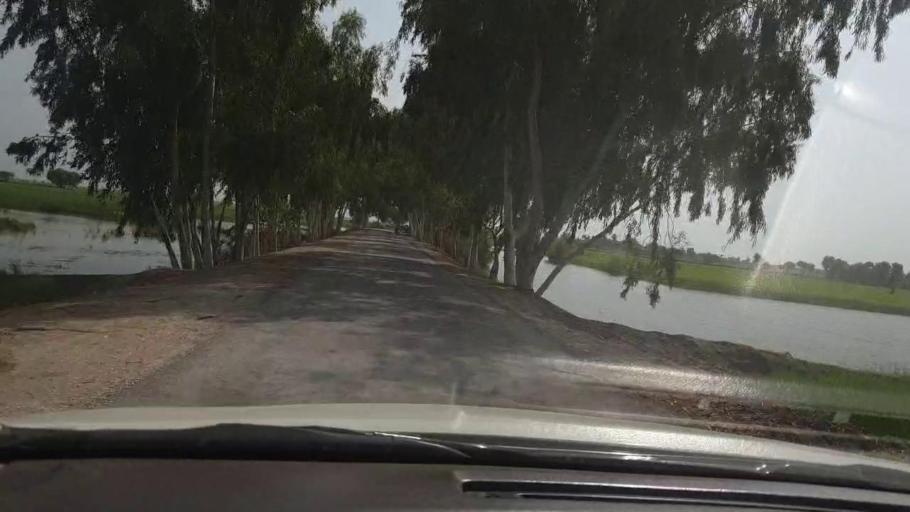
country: PK
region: Sindh
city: Rustam jo Goth
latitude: 27.9758
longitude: 68.7898
